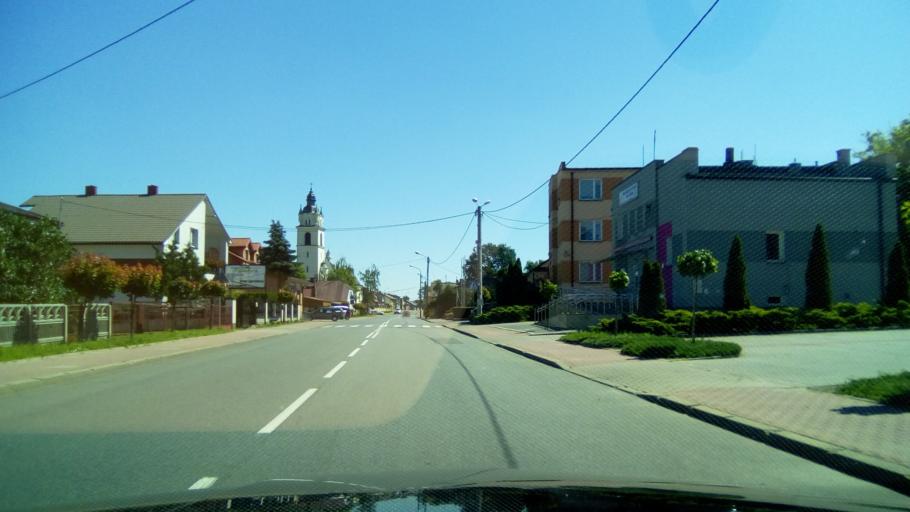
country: PL
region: Masovian Voivodeship
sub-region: Powiat przysuski
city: Klwow
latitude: 51.5332
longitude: 20.6316
